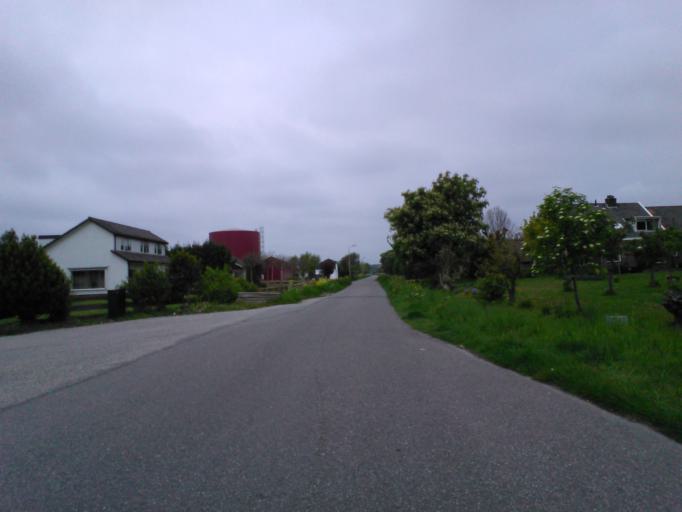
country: NL
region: South Holland
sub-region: Gemeente Pijnacker-Nootdorp
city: Pijnacker
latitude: 52.0422
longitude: 4.4329
